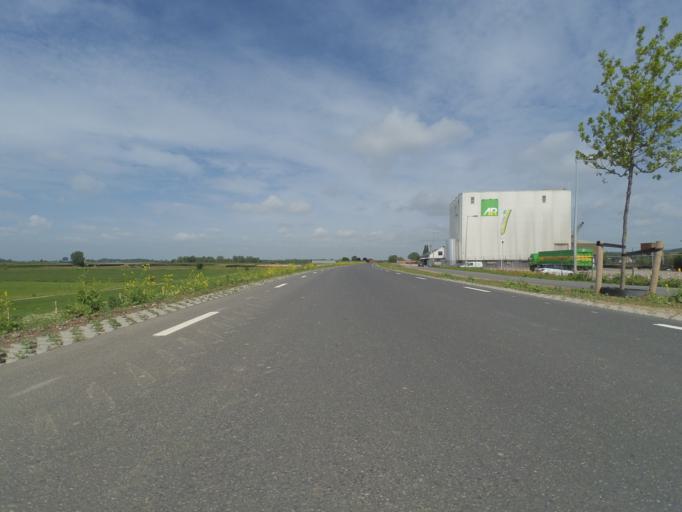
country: NL
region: Utrecht
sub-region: Gemeente Rhenen
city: Rhenen
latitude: 51.9498
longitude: 5.5647
